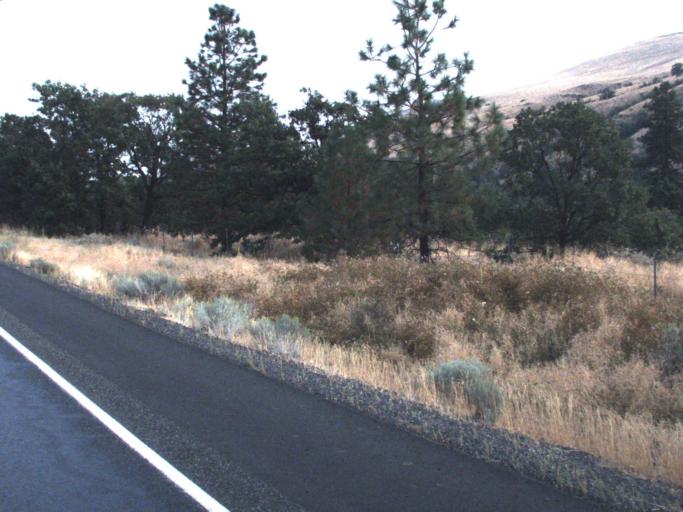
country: US
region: Washington
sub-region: Klickitat County
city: Goldendale
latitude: 46.0667
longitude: -120.5638
